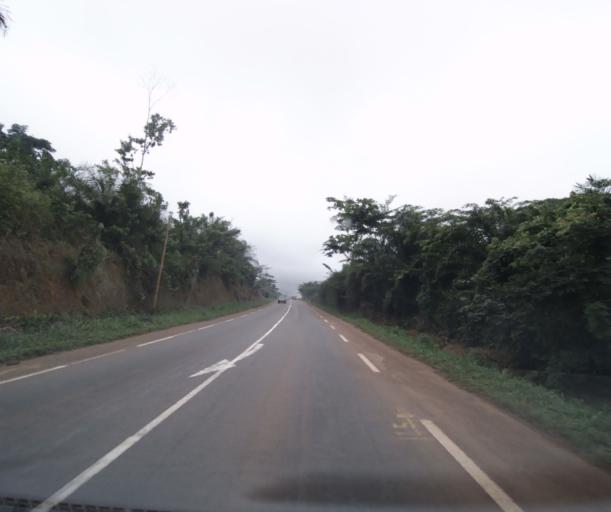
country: CM
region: Centre
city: Mbankomo
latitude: 3.7712
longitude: 11.1398
